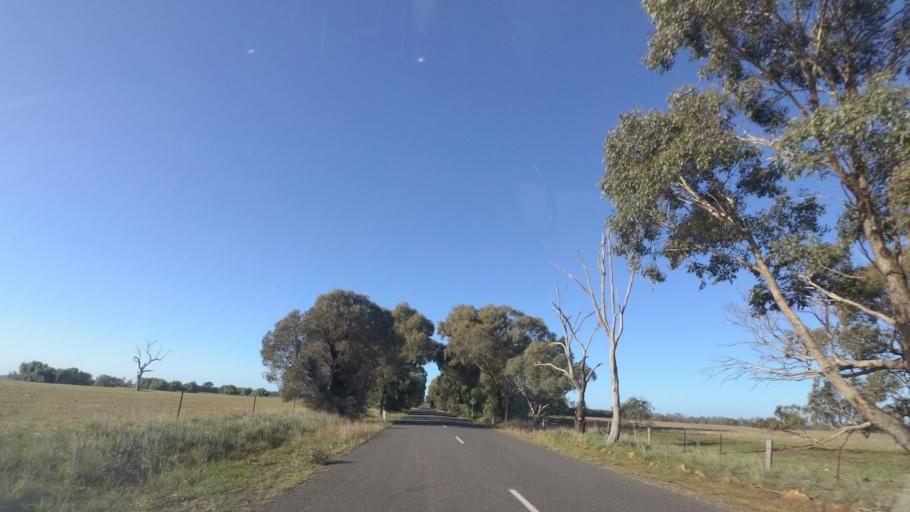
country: AU
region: Victoria
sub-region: Greater Bendigo
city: Epsom
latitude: -36.6490
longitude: 144.5259
